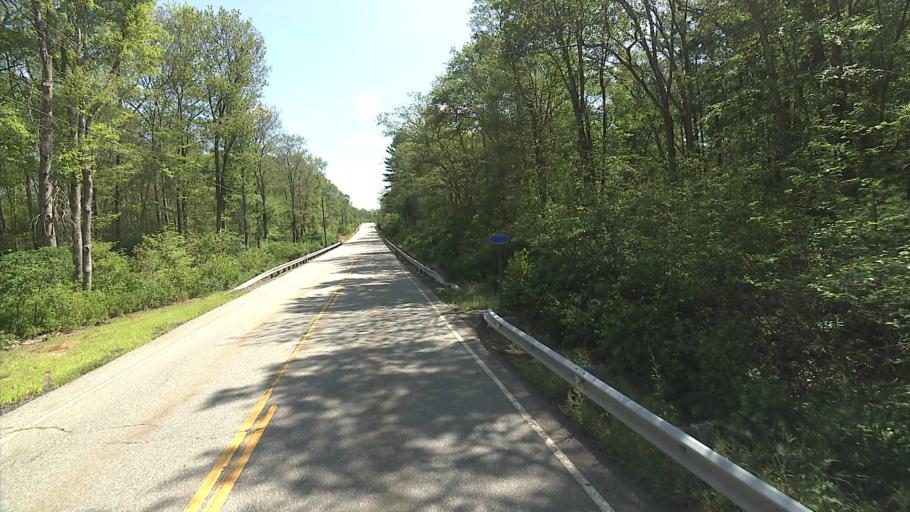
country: US
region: Rhode Island
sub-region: Washington County
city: Hopkinton
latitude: 41.5582
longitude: -71.8032
